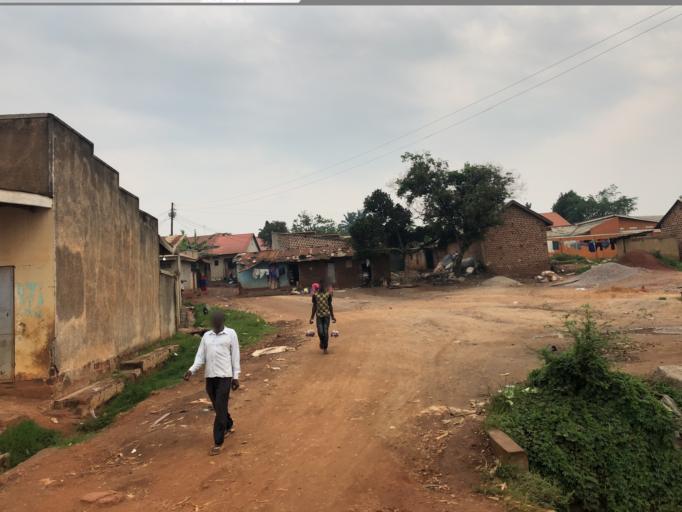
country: UG
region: Central Region
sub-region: Mukono District
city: Mukono
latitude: 0.3481
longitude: 32.7629
